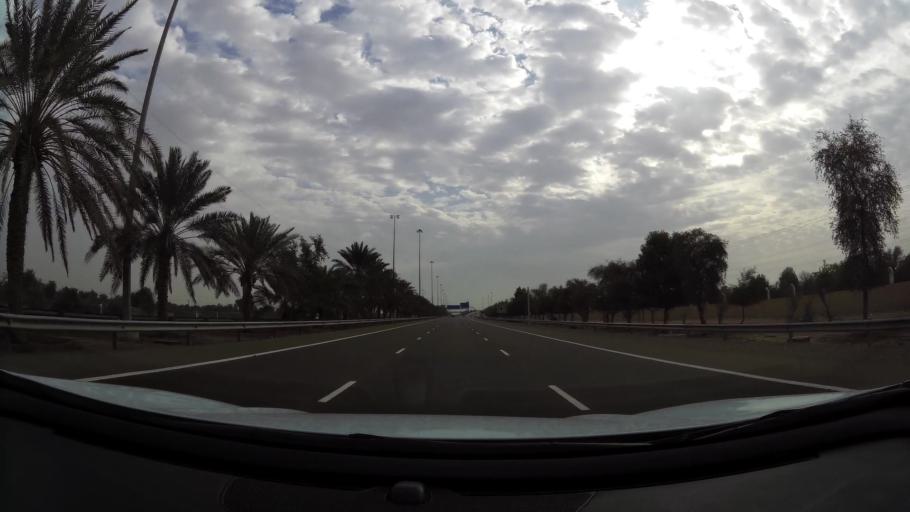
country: AE
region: Abu Dhabi
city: Al Ain
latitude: 24.2099
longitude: 55.4550
